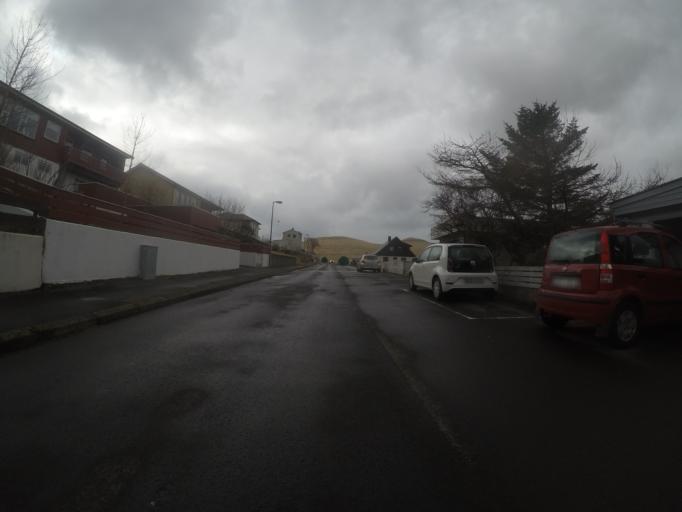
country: FO
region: Vagar
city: Midvagur
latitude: 62.0526
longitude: -7.1481
